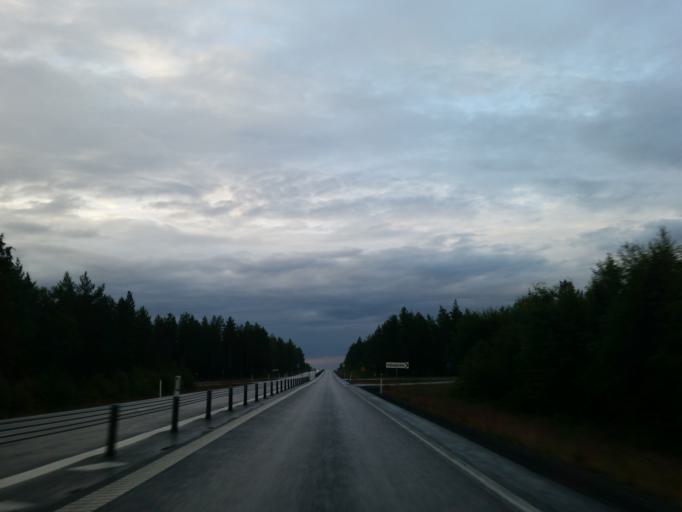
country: SE
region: Vaesterbotten
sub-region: Umea Kommun
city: Saevar
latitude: 63.9350
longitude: 20.6440
